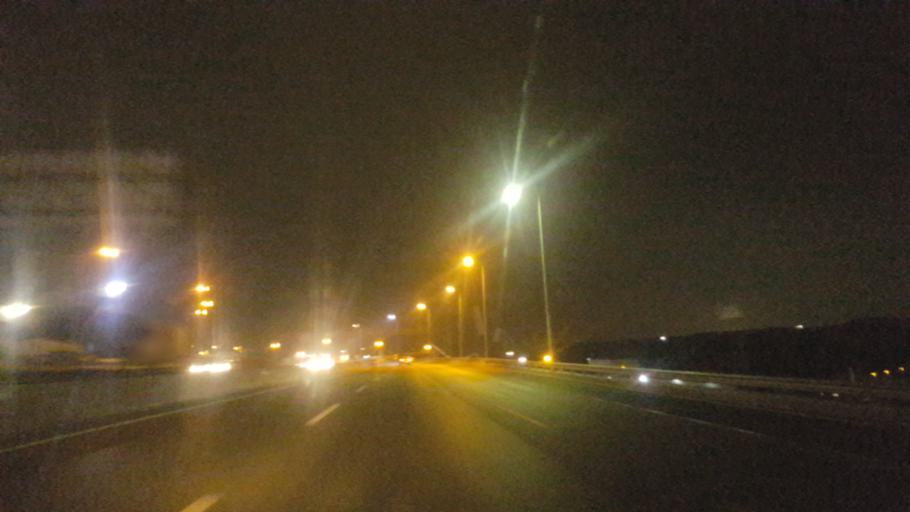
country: TR
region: Kocaeli
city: Tavsanli
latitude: 40.7934
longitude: 29.5266
